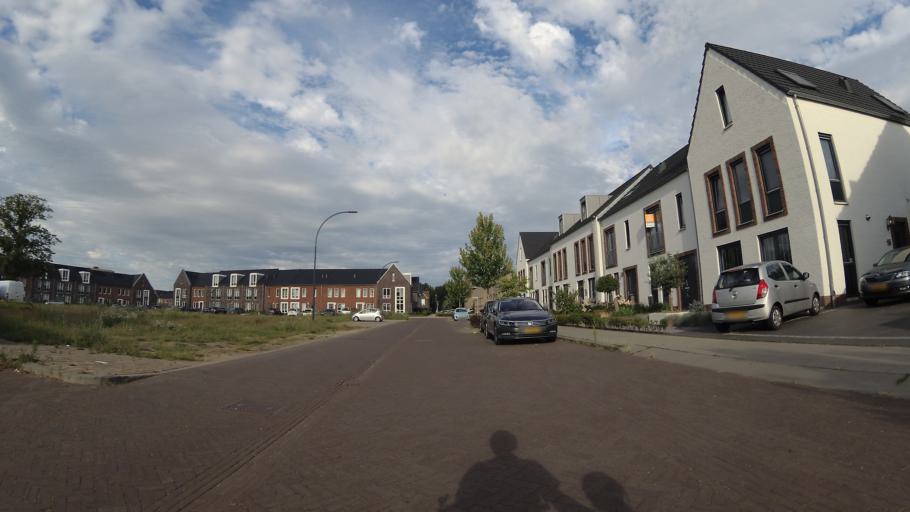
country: NL
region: North Brabant
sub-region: Gemeente Oosterhout
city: Oosterhout
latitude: 51.6486
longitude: 4.8289
